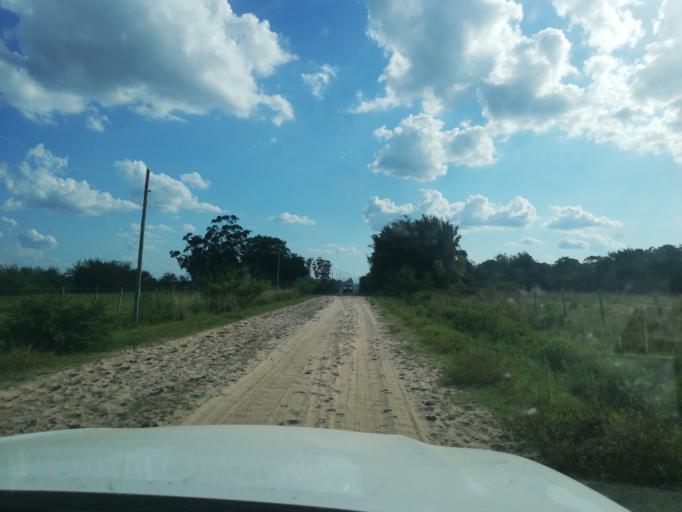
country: AR
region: Corrientes
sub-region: Departamento de San Miguel
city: San Miguel
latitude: -27.9939
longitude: -57.5772
